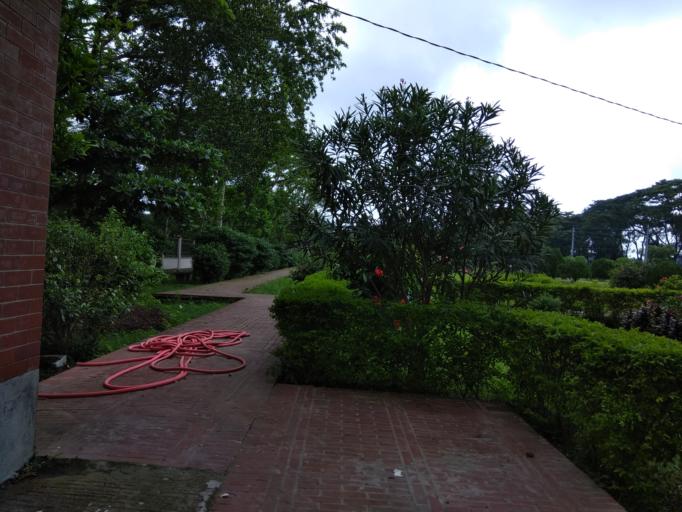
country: BD
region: Khulna
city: Khulna
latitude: 22.6735
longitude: 89.7422
